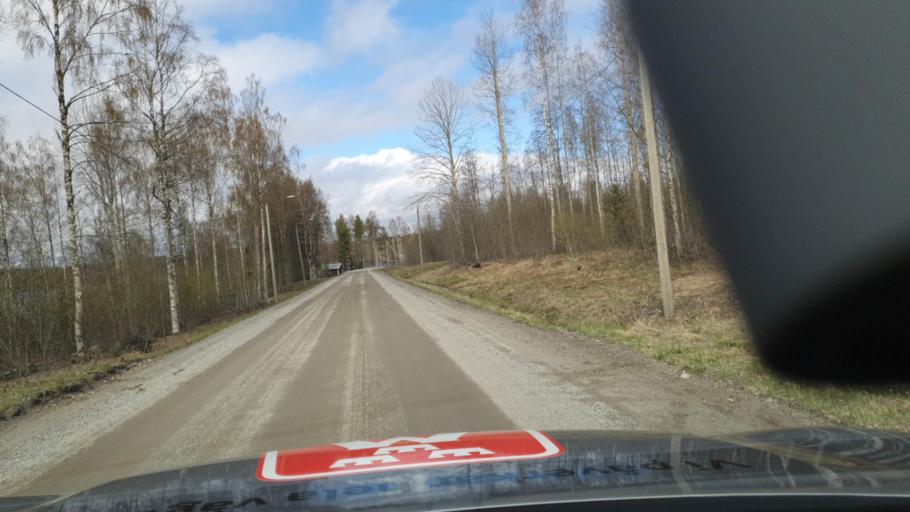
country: SE
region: Vaesterbotten
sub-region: Bjurholms Kommun
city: Bjurholm
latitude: 63.6890
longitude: 18.9581
